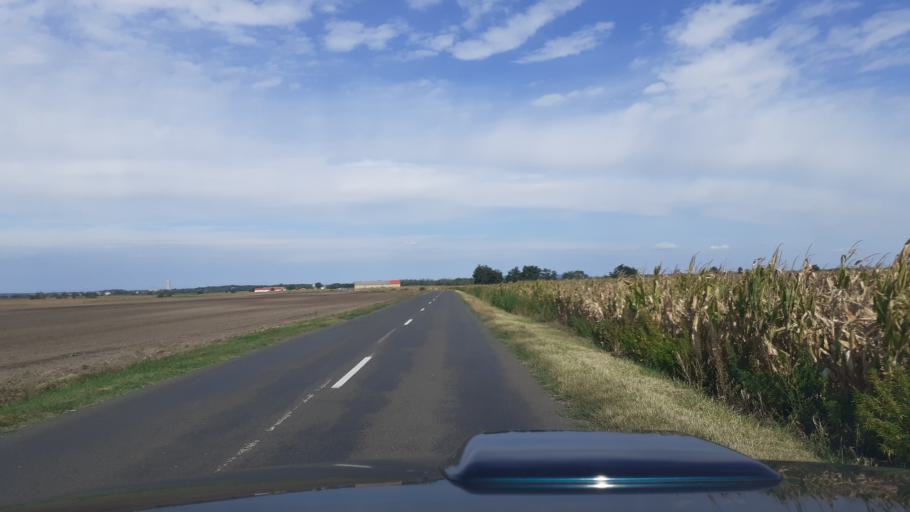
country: HU
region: Fejer
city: Pusztaszabolcs
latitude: 47.1108
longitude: 18.7040
